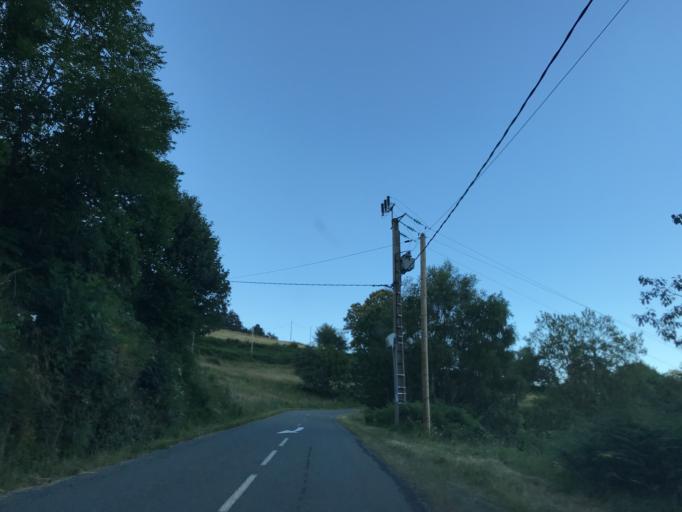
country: FR
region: Rhone-Alpes
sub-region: Departement de la Loire
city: Sail-sous-Couzan
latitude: 45.7361
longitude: 3.8680
